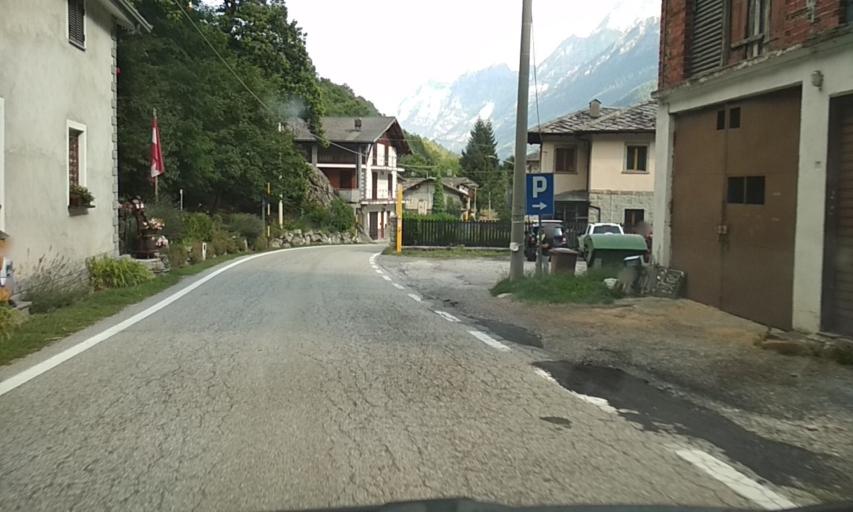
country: IT
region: Piedmont
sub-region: Provincia di Torino
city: Noasca
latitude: 45.4522
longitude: 7.3175
